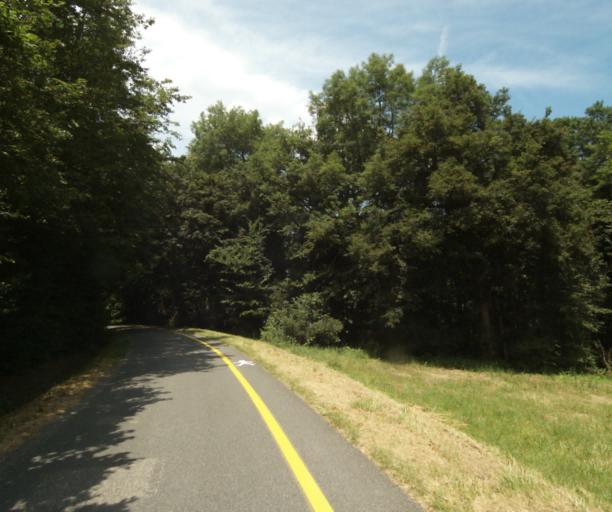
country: FR
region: Rhone-Alpes
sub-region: Departement de la Haute-Savoie
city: Chens-sur-Leman
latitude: 46.3220
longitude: 6.2629
